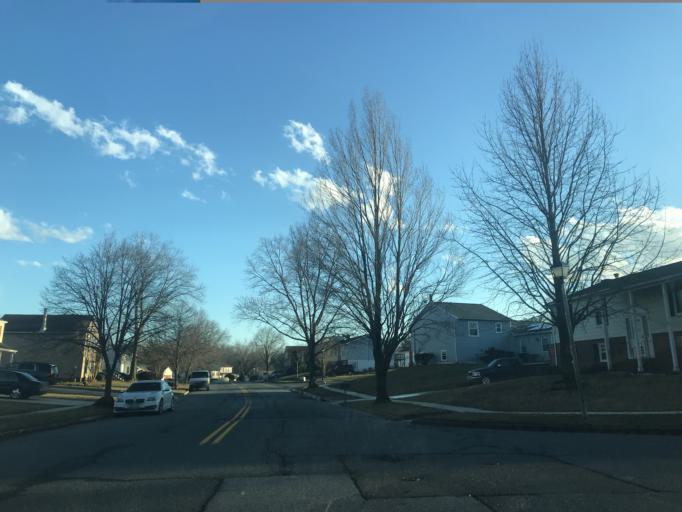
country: US
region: Maryland
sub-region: Prince George's County
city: Woodmore
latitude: 38.9066
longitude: -76.7922
